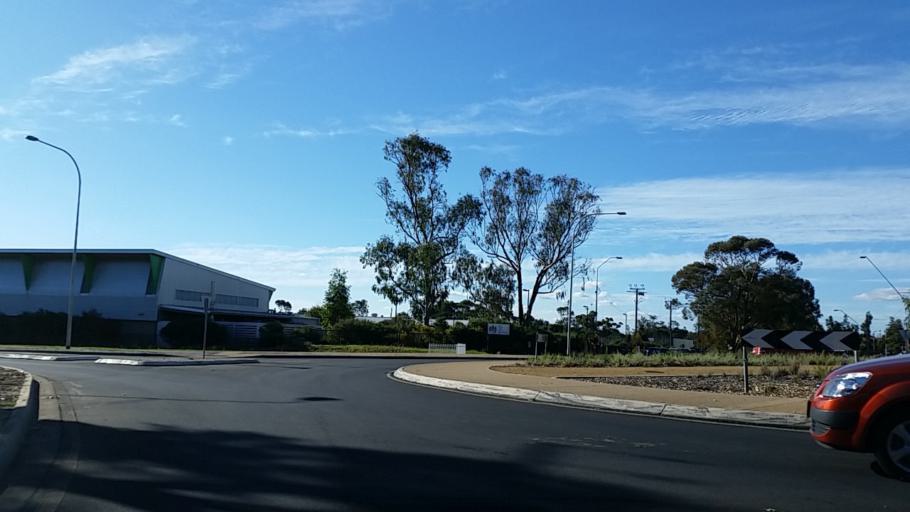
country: AU
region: South Australia
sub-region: Playford
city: Smithfield
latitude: -34.6813
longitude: 138.6729
